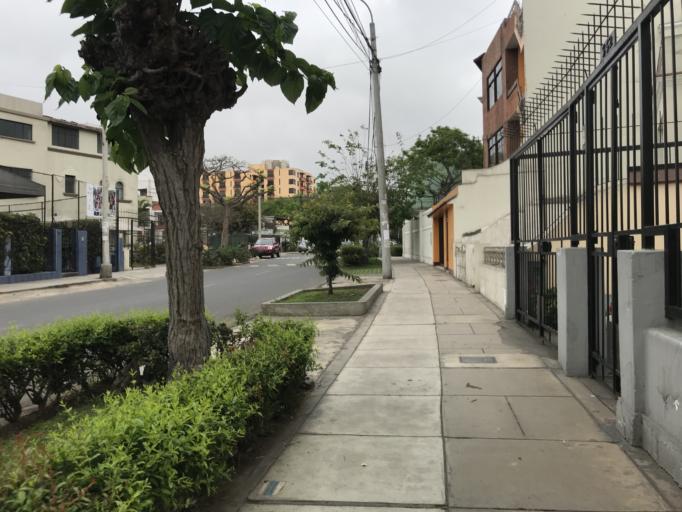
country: PE
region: Lima
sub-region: Lima
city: San Isidro
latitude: -12.0834
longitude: -77.0569
